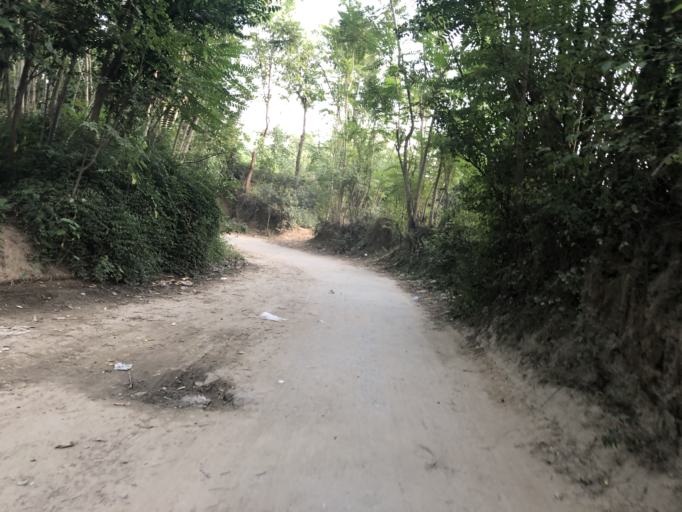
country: PK
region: Khyber Pakhtunkhwa
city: Daggar
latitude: 34.5795
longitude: 72.4552
